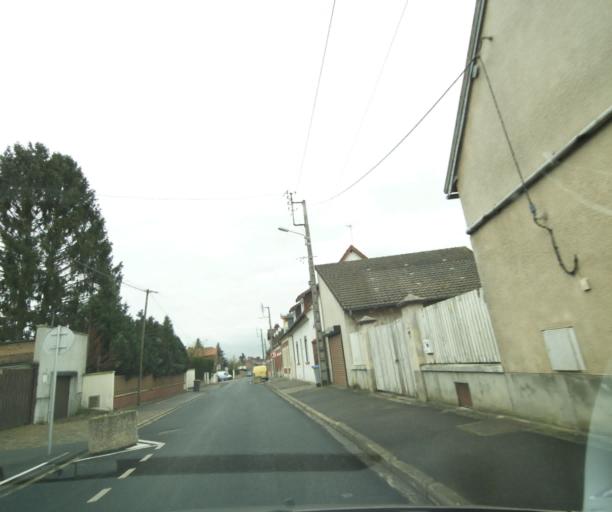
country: FR
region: Picardie
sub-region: Departement de l'Oise
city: Noyon
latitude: 49.5874
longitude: 3.0097
